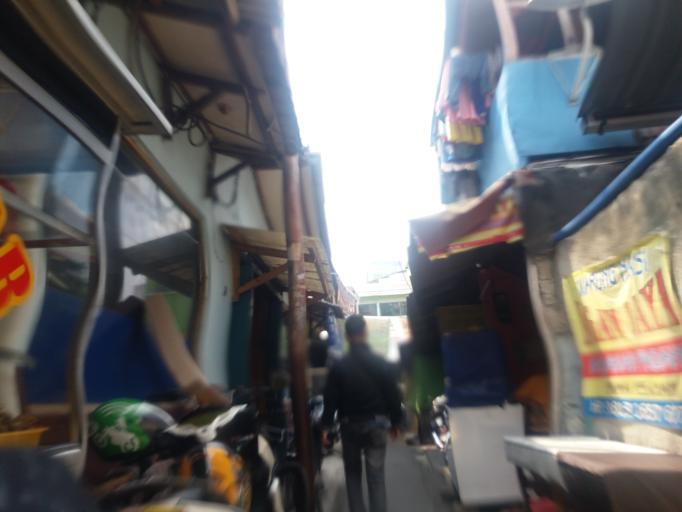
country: ID
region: Jakarta Raya
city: Jakarta
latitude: -6.2234
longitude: 106.8276
